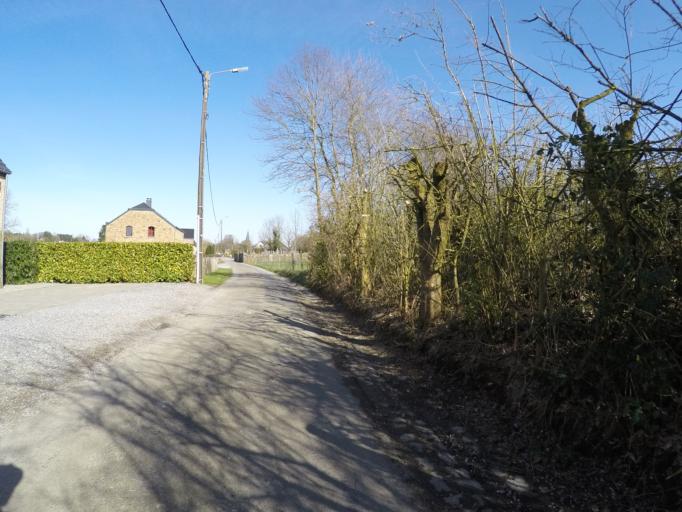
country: BE
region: Wallonia
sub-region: Province de Namur
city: Hamois
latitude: 50.3556
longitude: 5.1183
